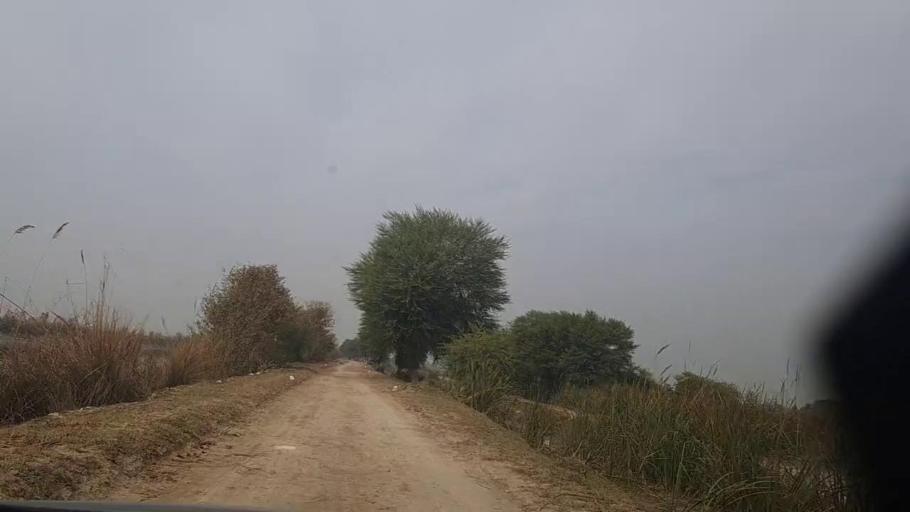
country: PK
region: Sindh
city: Daur
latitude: 26.3137
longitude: 68.2043
